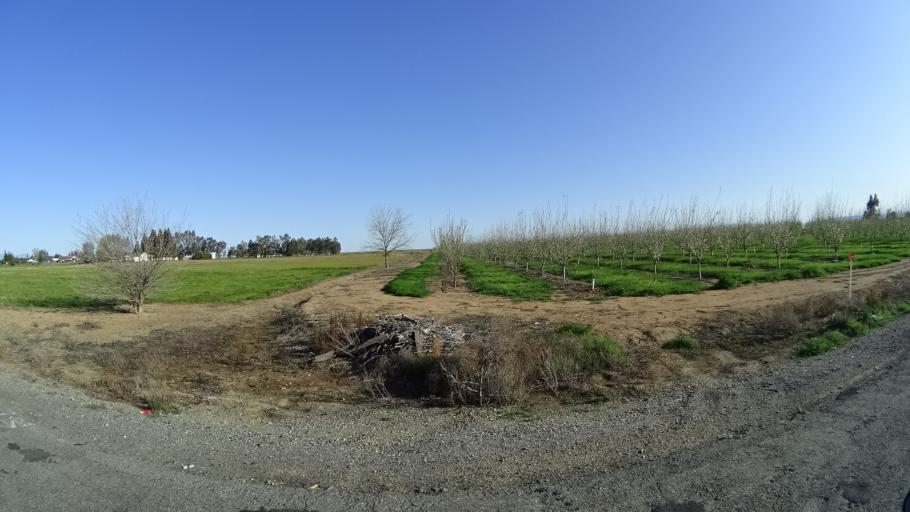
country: US
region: California
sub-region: Glenn County
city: Orland
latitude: 39.7976
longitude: -122.1456
